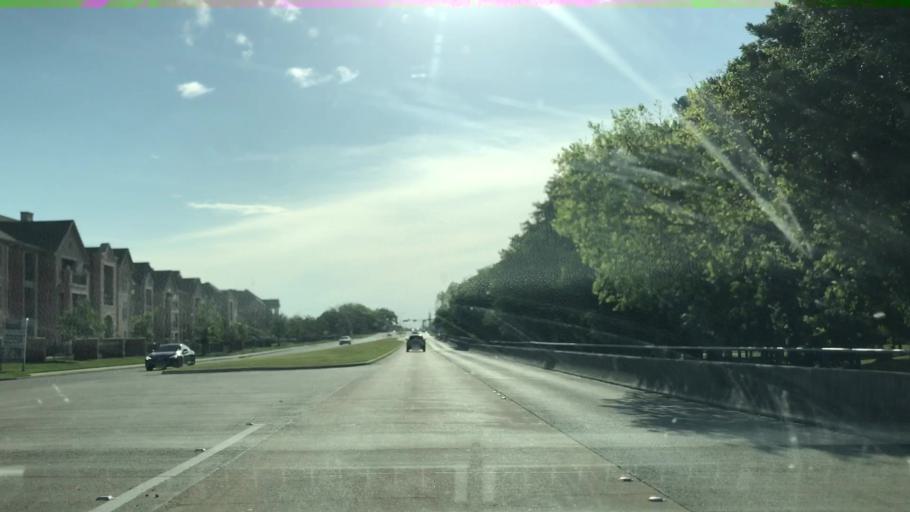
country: US
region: Texas
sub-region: Dallas County
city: Farmers Branch
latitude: 32.8955
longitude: -96.9216
